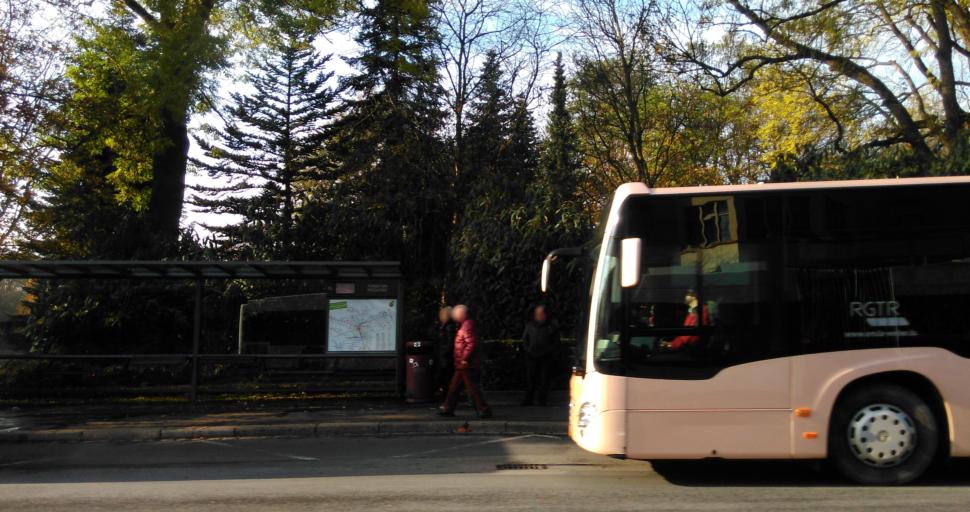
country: LU
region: Luxembourg
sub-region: Canton de Luxembourg
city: Luxembourg
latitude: 49.6161
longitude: 6.1266
